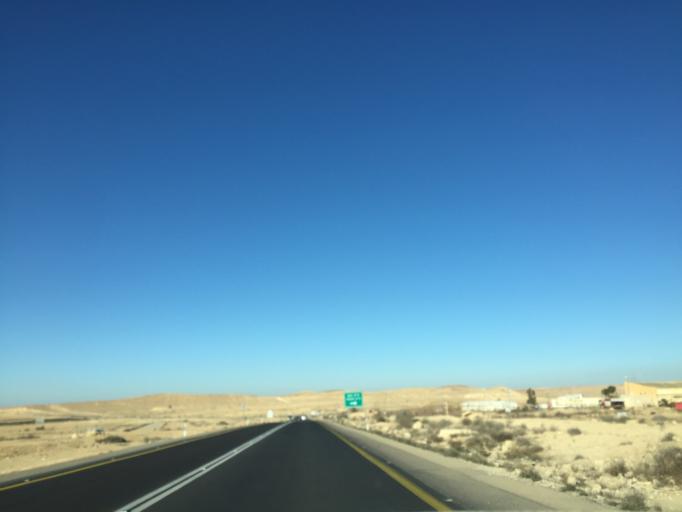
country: IL
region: Southern District
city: Mitzpe Ramon
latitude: 30.6503
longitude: 34.8096
